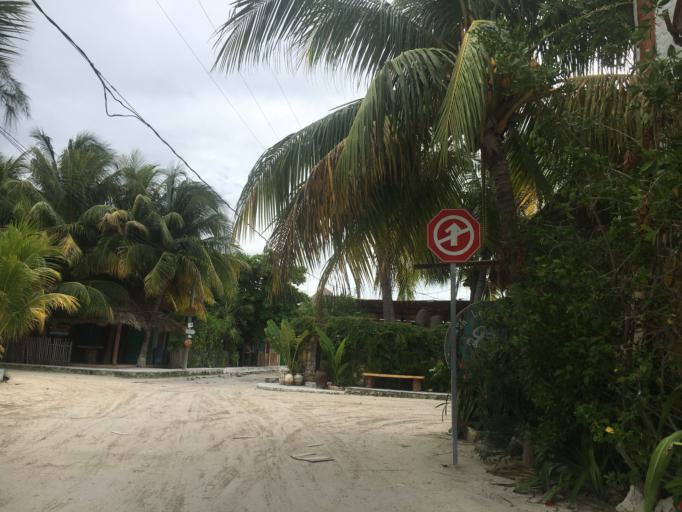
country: MX
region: Quintana Roo
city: Kantunilkin
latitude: 21.5256
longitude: -87.3778
